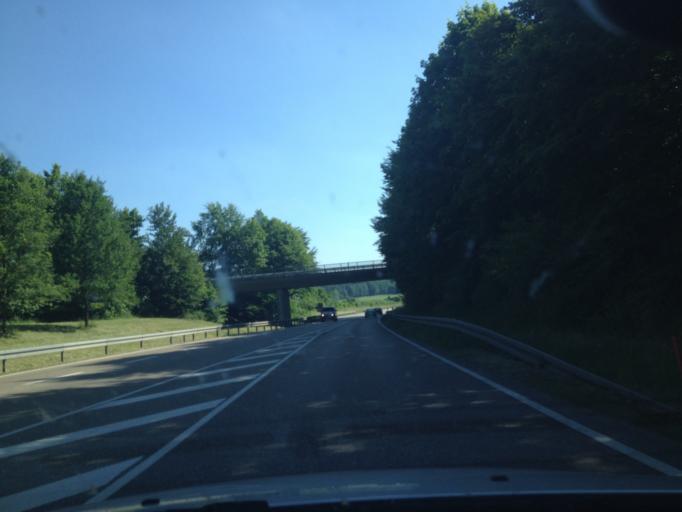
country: DE
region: Bavaria
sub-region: Swabia
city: Kuhbach
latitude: 48.4949
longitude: 11.2050
